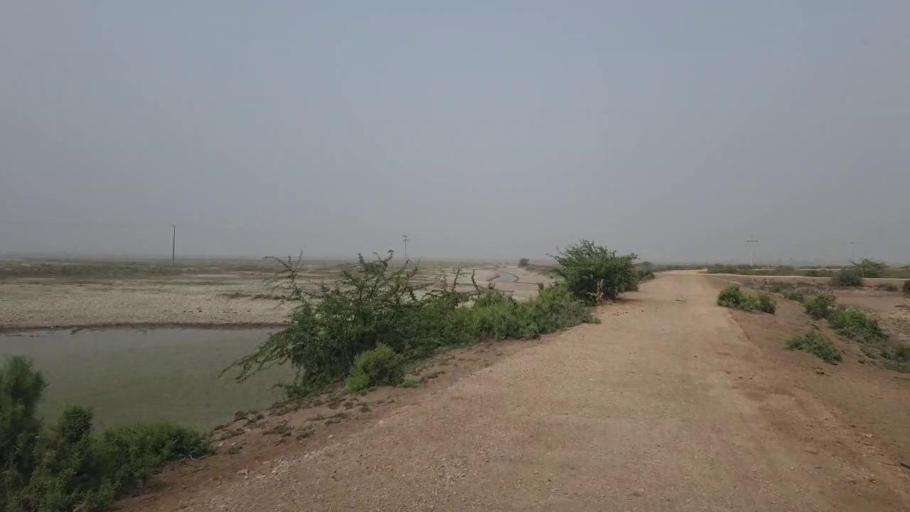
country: PK
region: Sindh
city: Kario
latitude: 24.6652
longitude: 68.6472
